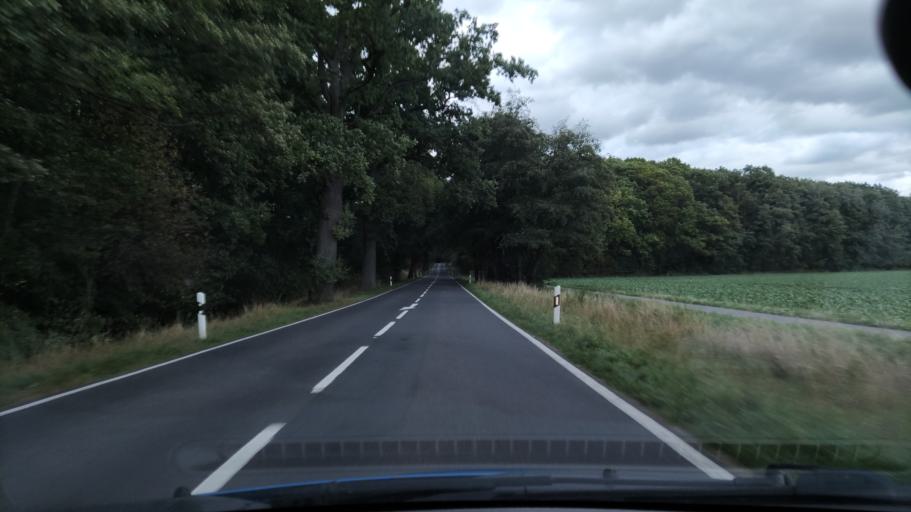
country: DE
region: Mecklenburg-Vorpommern
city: Lubtheen
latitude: 53.3756
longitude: 10.9655
